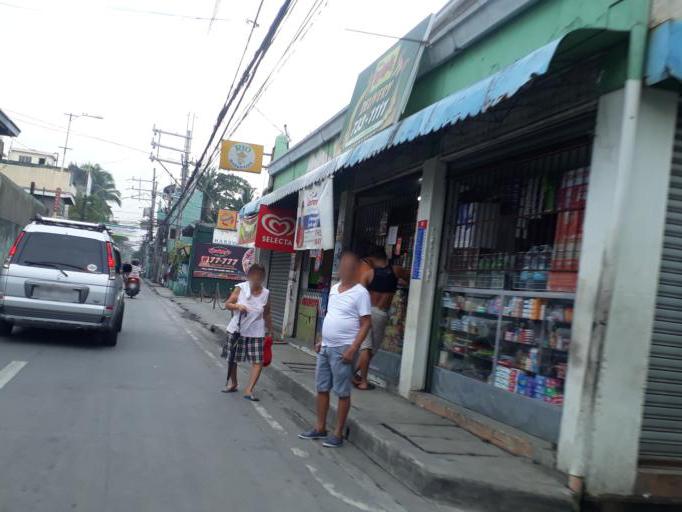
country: PH
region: Calabarzon
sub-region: Province of Rizal
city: Malabon
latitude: 14.6652
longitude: 120.9417
